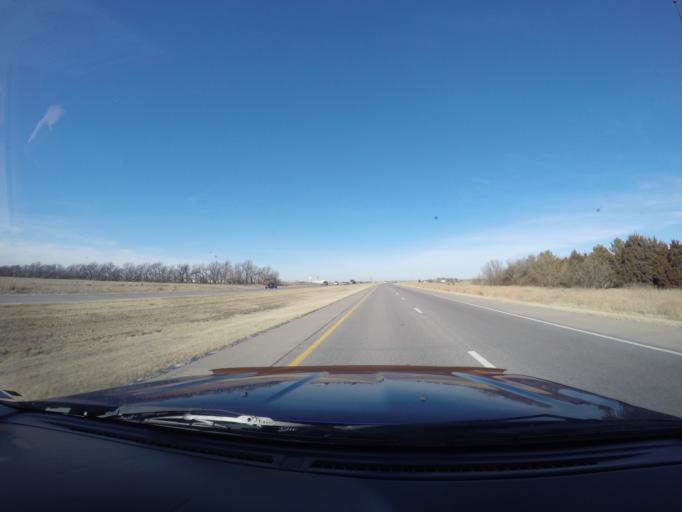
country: US
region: Kansas
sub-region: Harvey County
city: Newton
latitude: 37.9910
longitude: -97.3278
